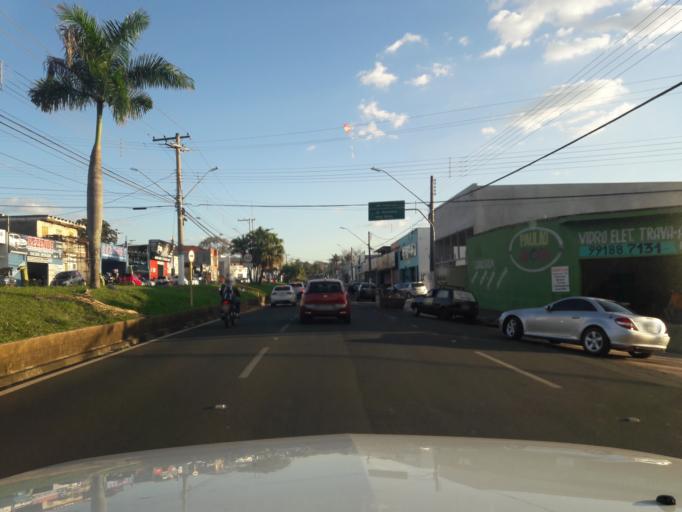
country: BR
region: Sao Paulo
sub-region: Moji-Guacu
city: Mogi-Gaucu
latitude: -22.3937
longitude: -46.9462
